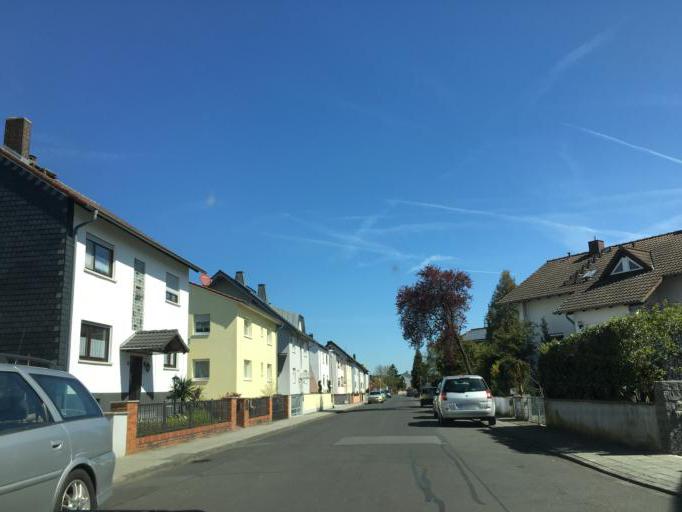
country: DE
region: Hesse
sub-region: Regierungsbezirk Darmstadt
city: Gross-Zimmern
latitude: 49.8780
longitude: 8.8149
